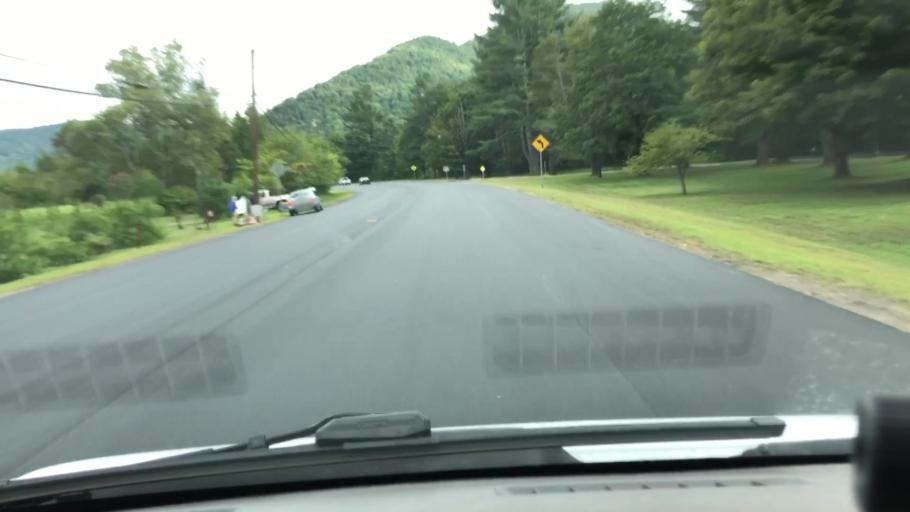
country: US
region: Massachusetts
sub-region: Franklin County
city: Charlemont
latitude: 42.6364
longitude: -72.9055
